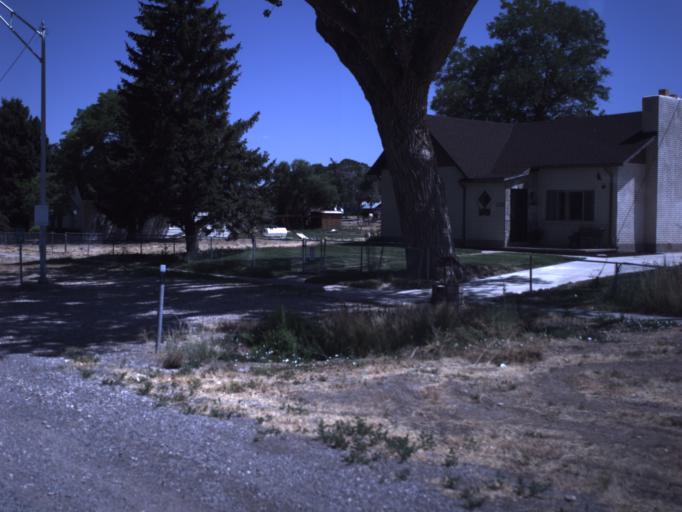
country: US
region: Utah
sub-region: Millard County
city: Delta
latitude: 39.3706
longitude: -112.3361
